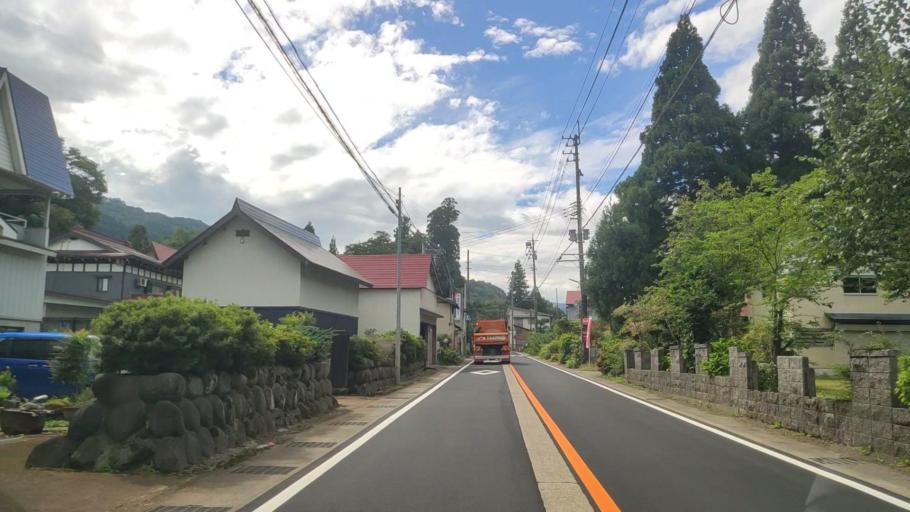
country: JP
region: Niigata
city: Arai
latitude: 36.9589
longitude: 138.2708
